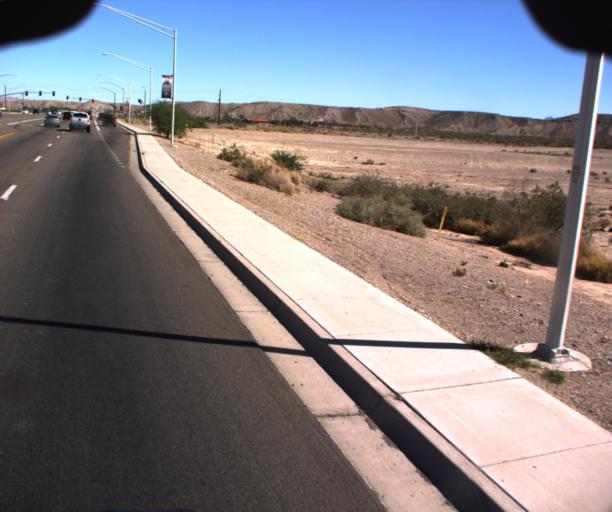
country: US
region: Arizona
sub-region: Mohave County
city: Bullhead City
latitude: 35.0544
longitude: -114.5890
